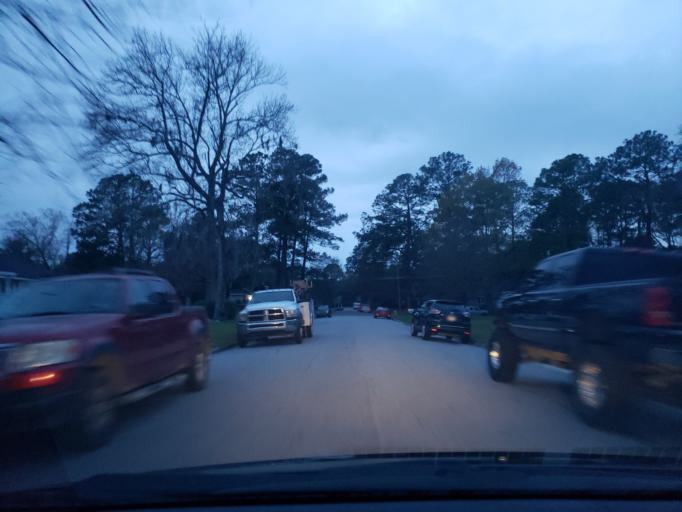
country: US
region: Georgia
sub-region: Chatham County
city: Thunderbolt
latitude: 32.0300
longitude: -81.1020
